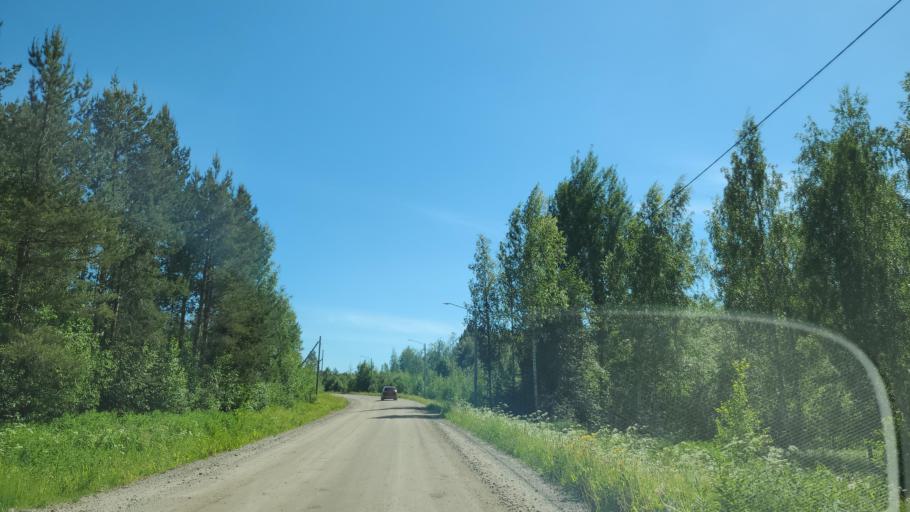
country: SE
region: Vaesterbotten
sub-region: Bjurholms Kommun
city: Bjurholm
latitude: 63.6894
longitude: 18.9580
